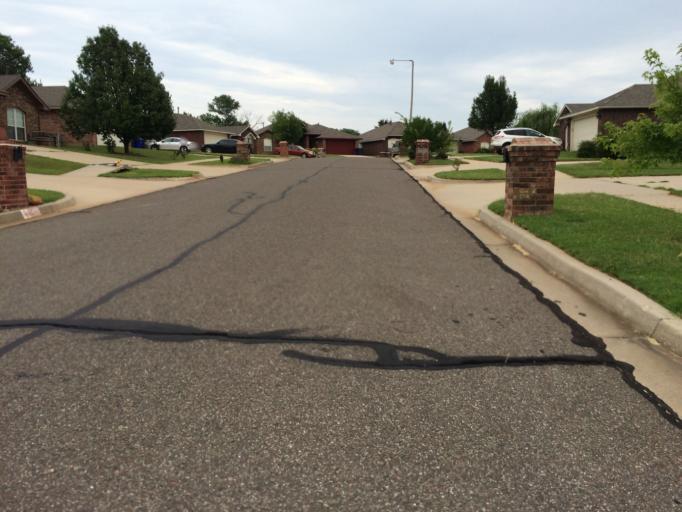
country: US
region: Oklahoma
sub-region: Cleveland County
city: Hall Park
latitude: 35.2515
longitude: -97.4207
